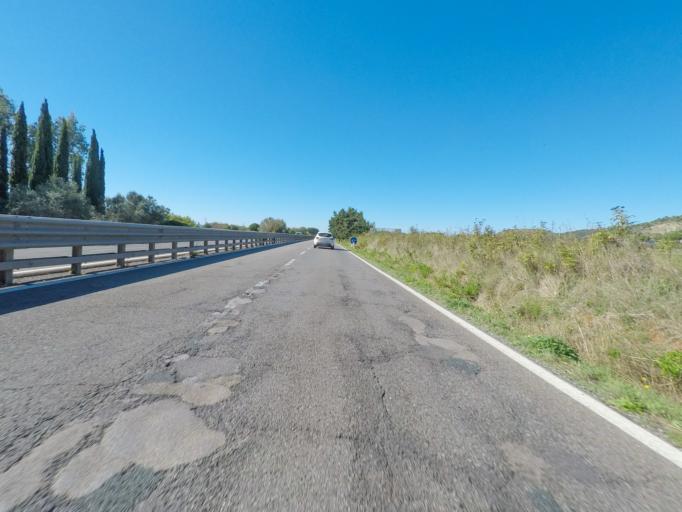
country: IT
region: Tuscany
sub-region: Provincia di Grosseto
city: Orbetello Scalo
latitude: 42.4384
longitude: 11.2743
